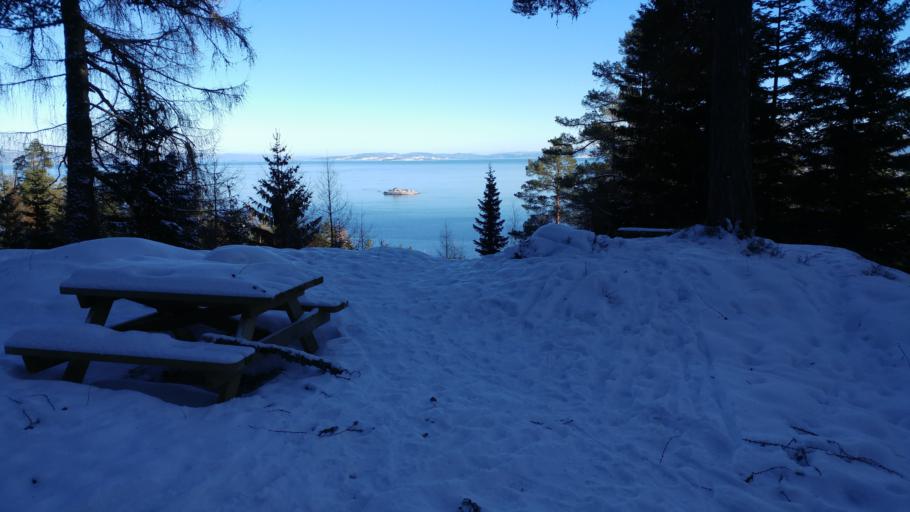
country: NO
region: Sor-Trondelag
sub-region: Trondheim
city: Trondheim
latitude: 63.4357
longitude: 10.3419
